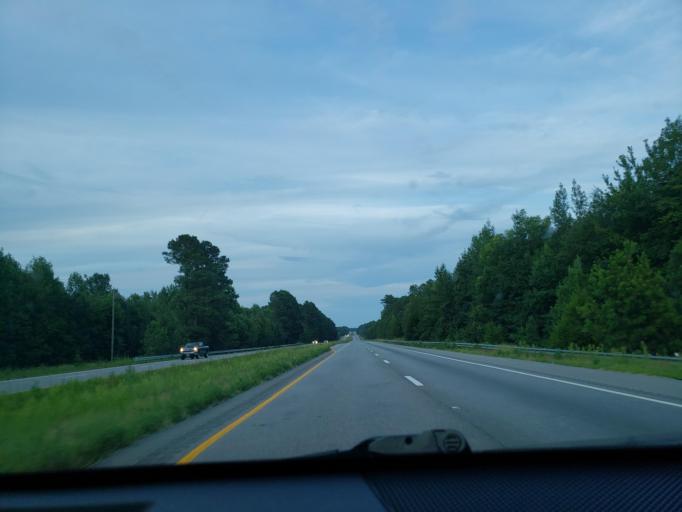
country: US
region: Virginia
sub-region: City of Emporia
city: Emporia
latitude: 36.6968
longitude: -77.3374
